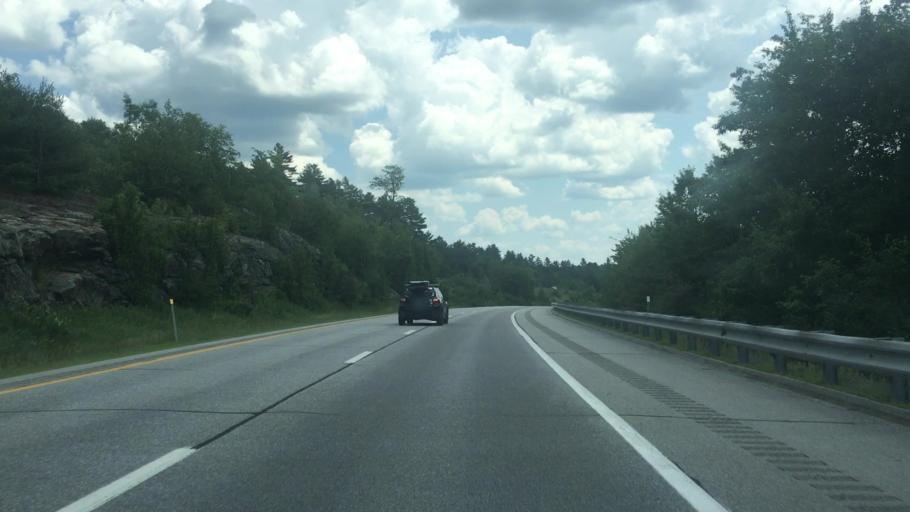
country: US
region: New Hampshire
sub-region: Merrimack County
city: New London
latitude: 43.4341
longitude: -72.0431
